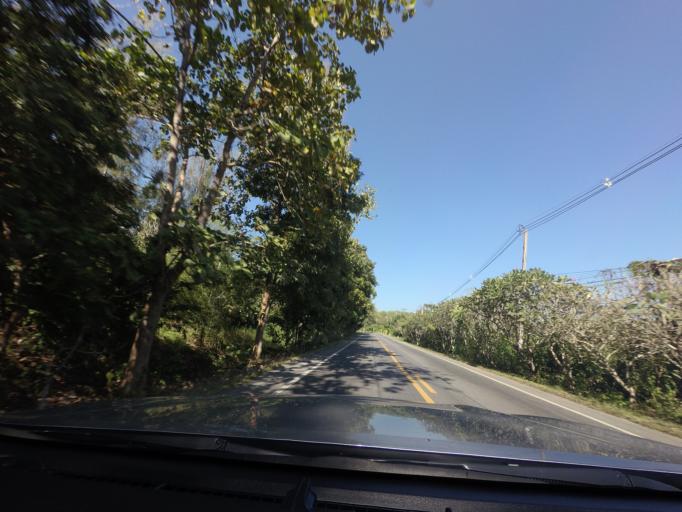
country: TH
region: Sukhothai
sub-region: Amphoe Si Satchanalai
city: Si Satchanalai
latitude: 17.6134
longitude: 99.7083
